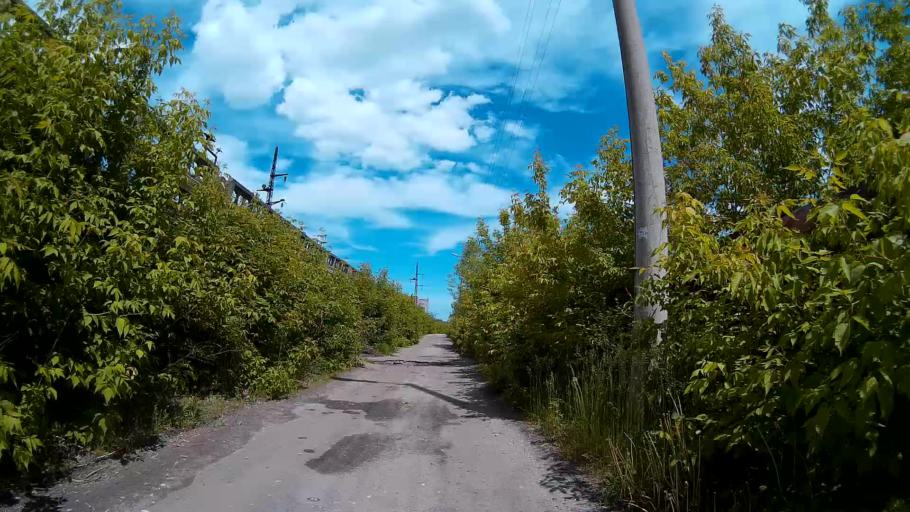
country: RU
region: Ulyanovsk
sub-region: Ulyanovskiy Rayon
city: Ulyanovsk
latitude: 54.2828
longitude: 48.3635
